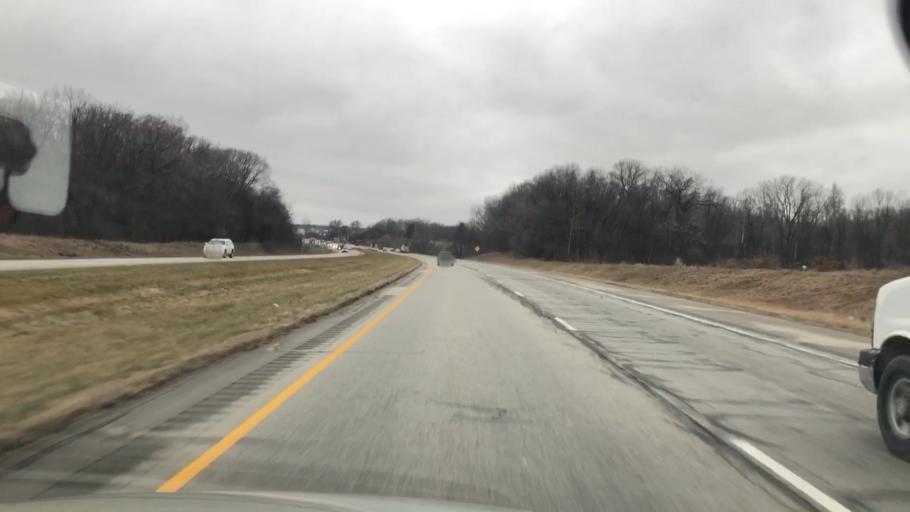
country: US
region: Indiana
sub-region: Kosciusko County
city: Warsaw
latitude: 41.2570
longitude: -85.8320
